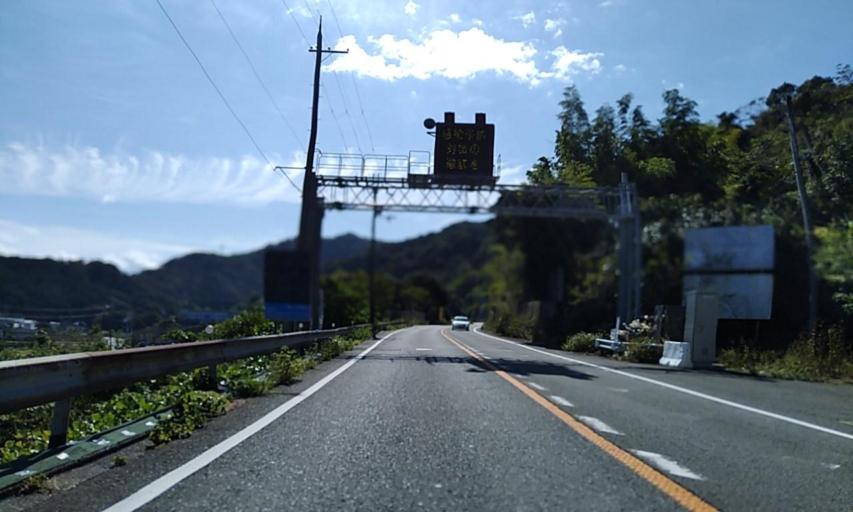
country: JP
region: Wakayama
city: Gobo
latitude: 34.0015
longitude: 135.1900
